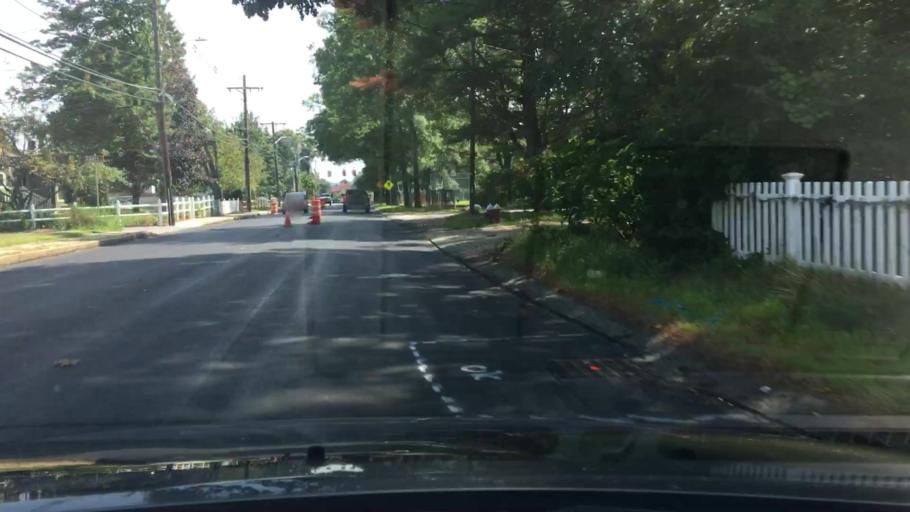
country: US
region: Massachusetts
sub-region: Worcester County
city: Milford
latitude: 42.1532
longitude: -71.5294
